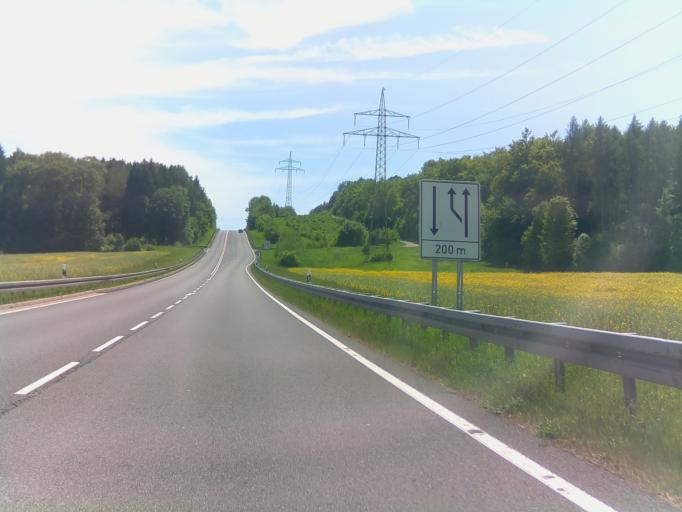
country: DE
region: Bavaria
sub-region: Regierungsbezirk Unterfranken
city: Nudlingen
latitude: 50.2007
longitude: 10.1616
